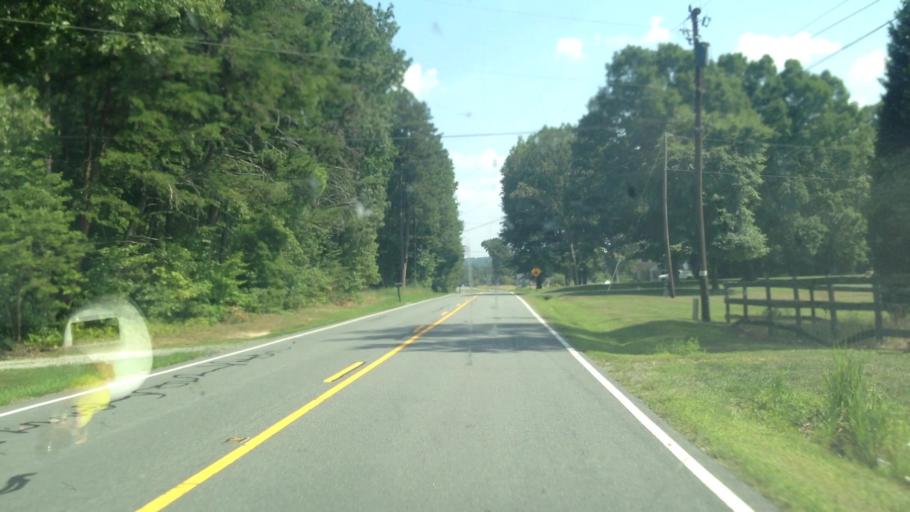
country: US
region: North Carolina
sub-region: Stokes County
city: Walnut Cove
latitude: 36.3439
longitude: -80.0527
